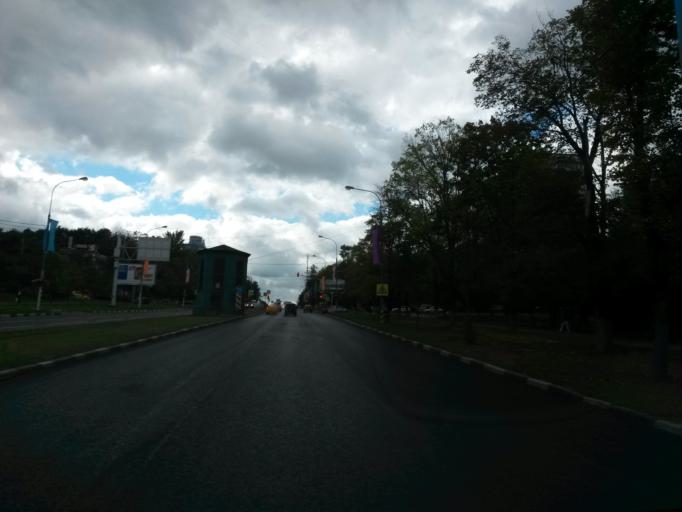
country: RU
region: Moskovskaya
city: Cheremushki
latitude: 55.6755
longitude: 37.5601
